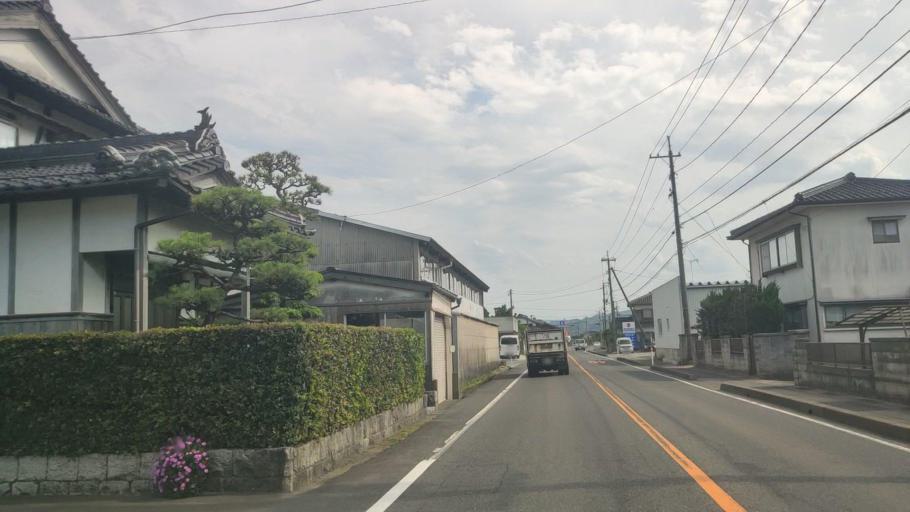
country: JP
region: Tottori
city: Tottori
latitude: 35.4736
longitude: 134.2047
